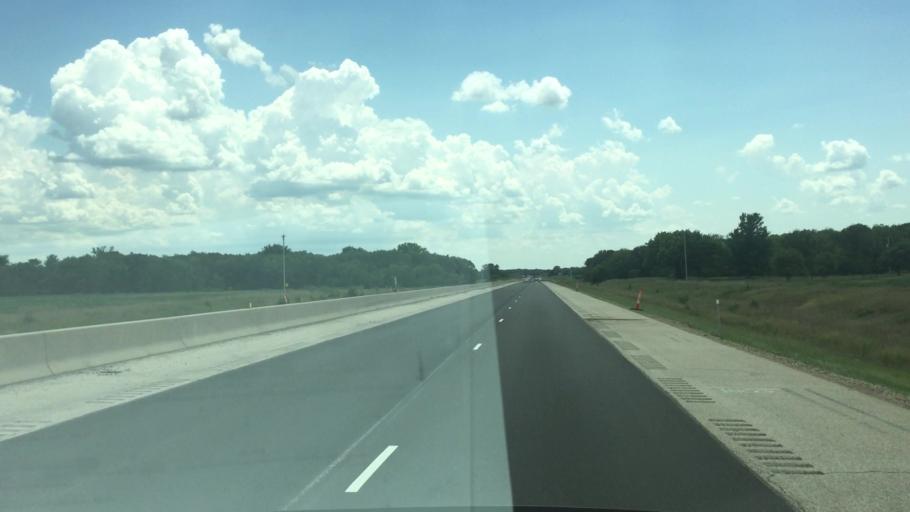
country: US
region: Kansas
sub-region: Lyon County
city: Emporia
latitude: 38.5227
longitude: -96.1414
